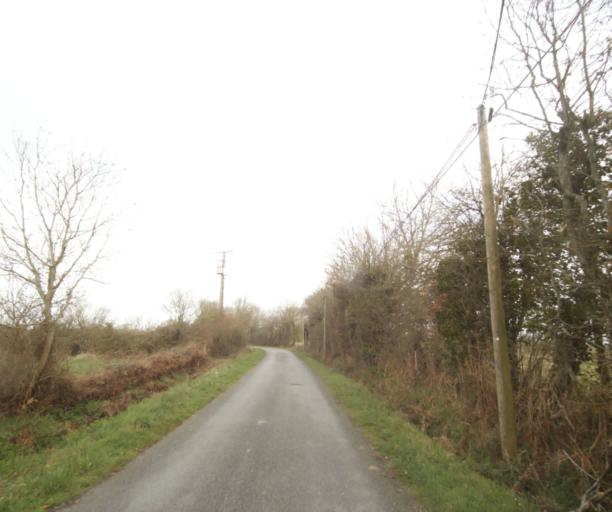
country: FR
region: Pays de la Loire
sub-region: Departement de la Loire-Atlantique
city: Bouvron
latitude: 47.4033
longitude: -1.8627
